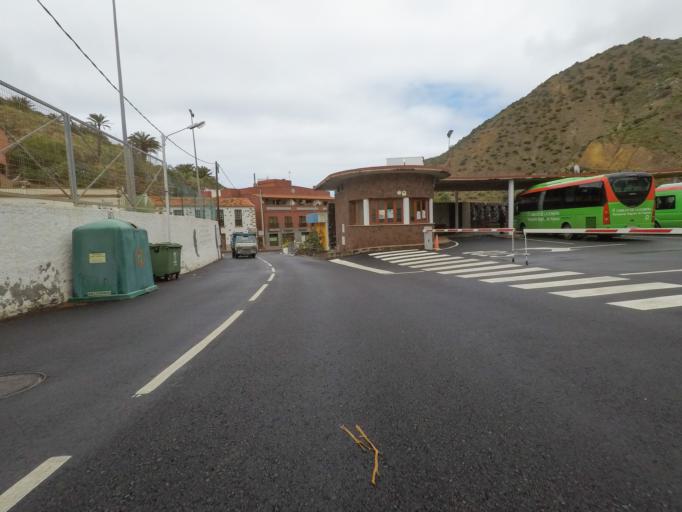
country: ES
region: Canary Islands
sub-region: Provincia de Santa Cruz de Tenerife
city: Vallehermosa
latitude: 28.1813
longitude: -17.2645
